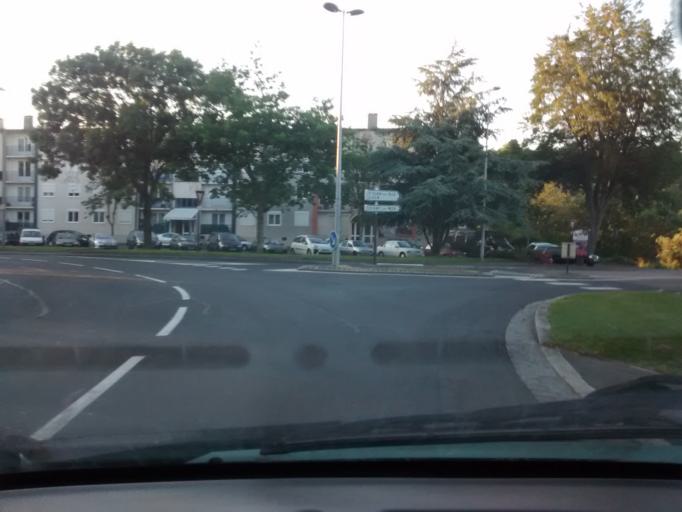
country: FR
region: Lower Normandy
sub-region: Departement de la Manche
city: Saint-Lo
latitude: 49.1179
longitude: -1.0831
